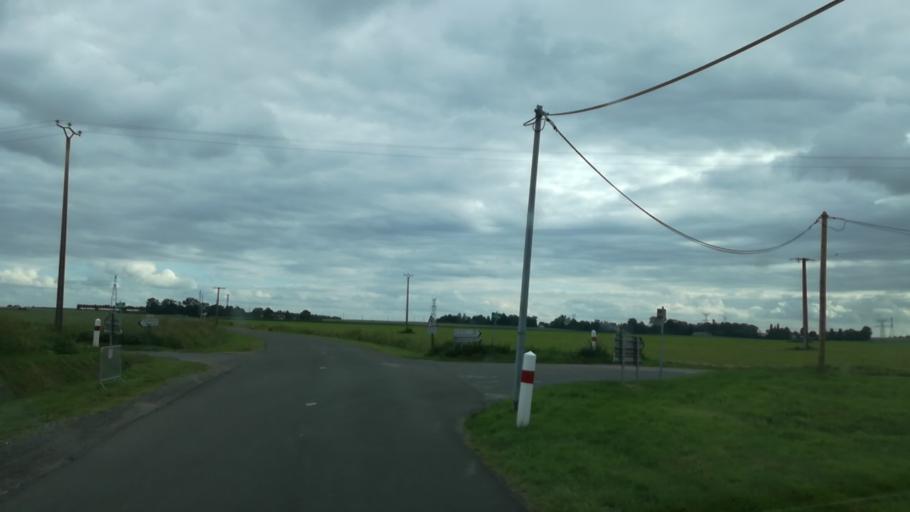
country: FR
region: Haute-Normandie
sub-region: Departement de l'Eure
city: Bourg-Achard
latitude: 49.3172
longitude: 0.8048
